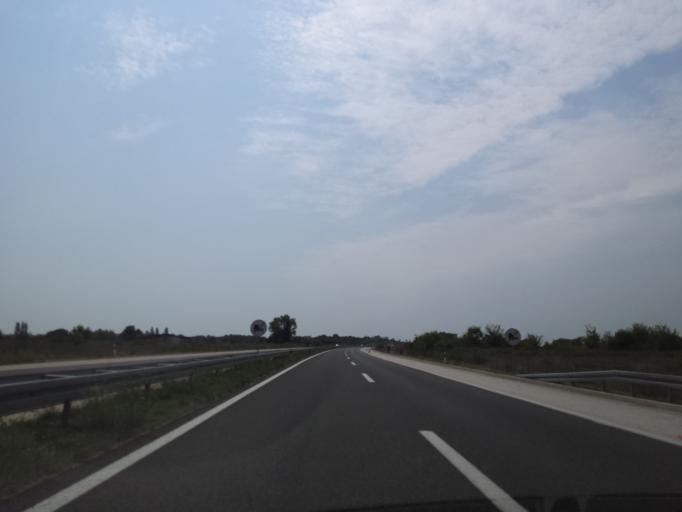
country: HR
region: Zadarska
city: Posedarje
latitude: 44.2015
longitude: 15.4432
